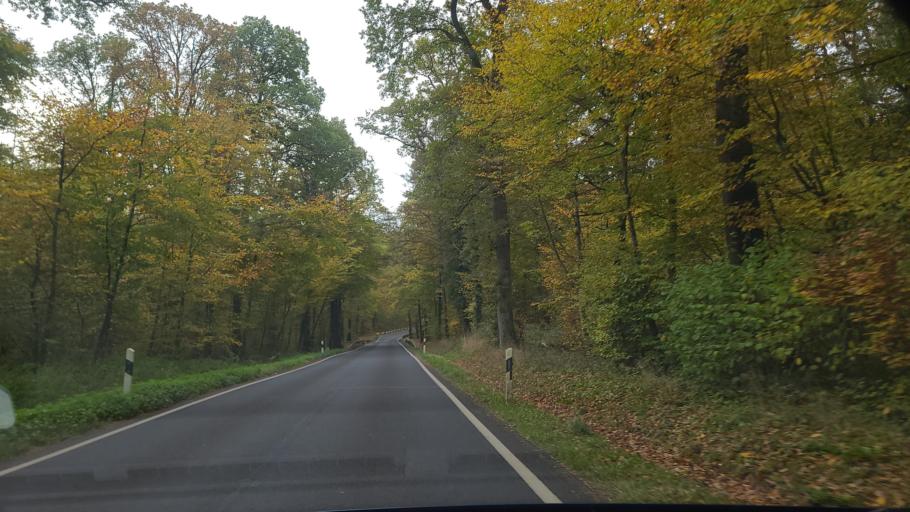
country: LU
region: Luxembourg
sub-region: Canton de Capellen
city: Dippach
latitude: 49.6057
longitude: 6.0011
